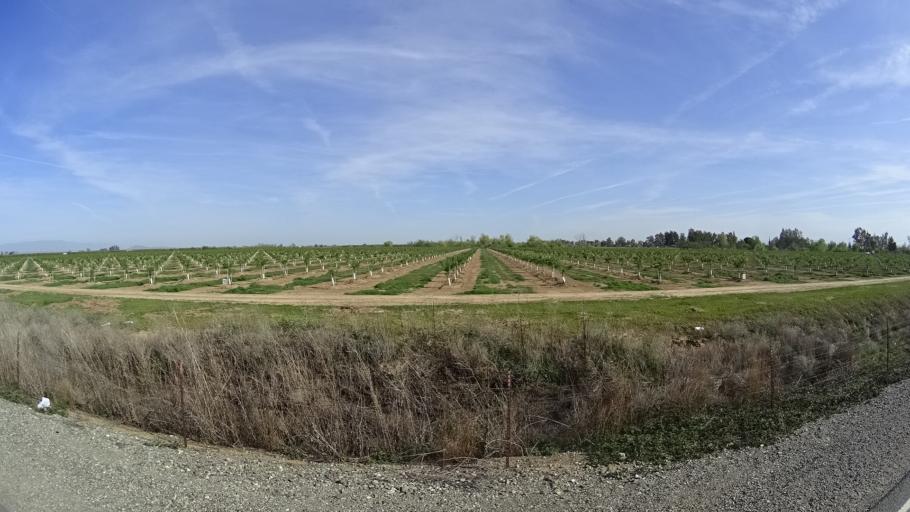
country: US
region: California
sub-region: Glenn County
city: Willows
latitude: 39.6241
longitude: -122.2014
